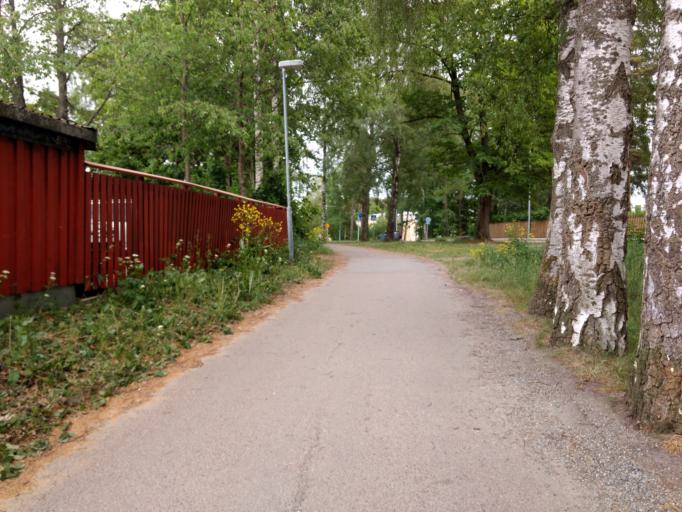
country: SE
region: Stockholm
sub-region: Upplands Vasby Kommun
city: Upplands Vaesby
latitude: 59.5235
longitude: 17.9121
